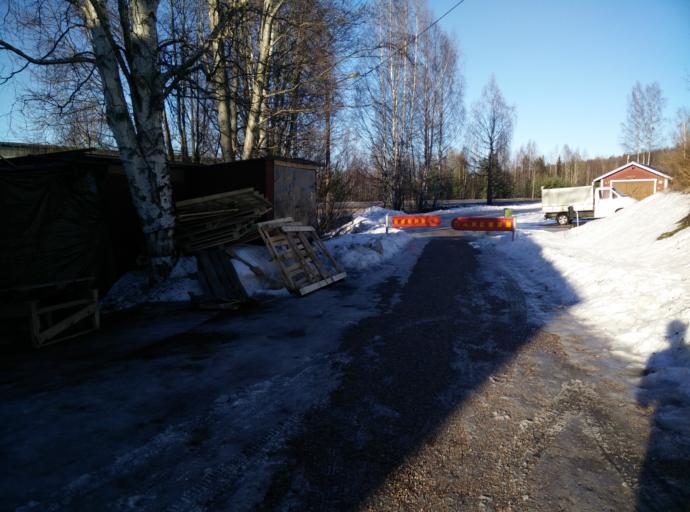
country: SE
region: Vaesternorrland
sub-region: Sundsvalls Kommun
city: Skottsund
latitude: 62.3093
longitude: 17.3894
